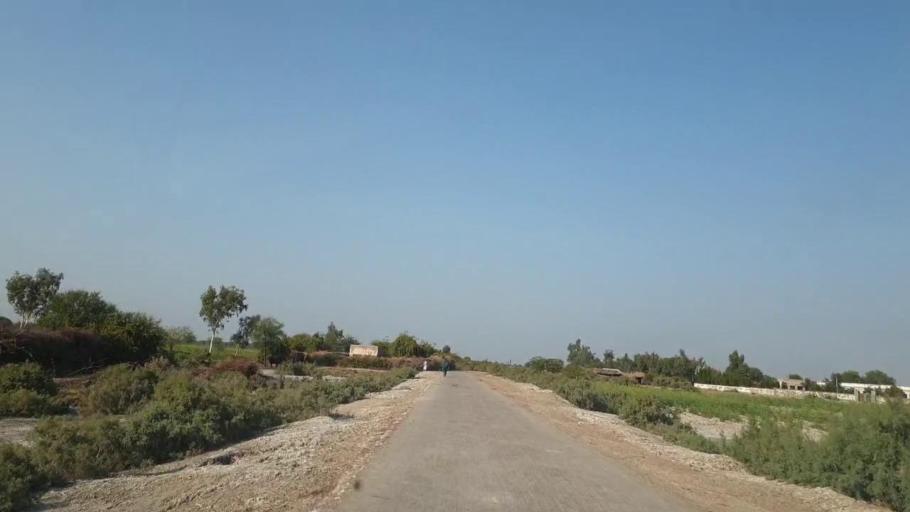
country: PK
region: Sindh
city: Tando Mittha Khan
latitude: 25.7534
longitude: 69.2006
